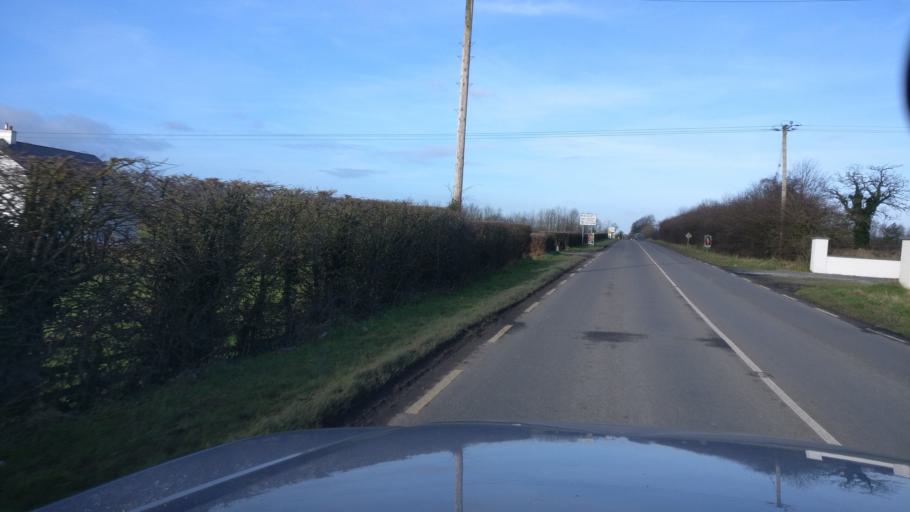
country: IE
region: Leinster
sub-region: Laois
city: Portlaoise
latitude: 53.0126
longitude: -7.2749
